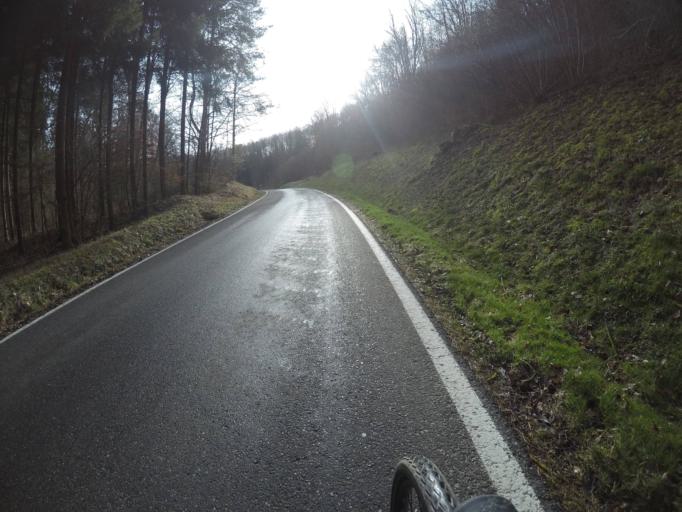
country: DE
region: Baden-Wuerttemberg
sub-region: Karlsruhe Region
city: Calw
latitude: 48.6818
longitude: 8.7700
